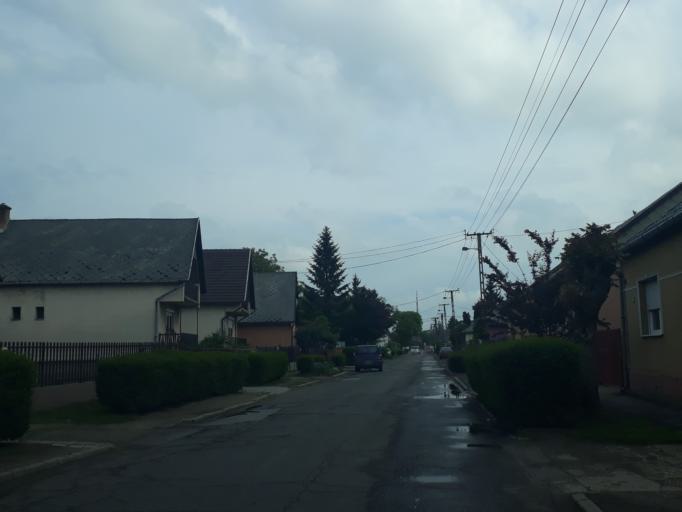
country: HU
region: Szabolcs-Szatmar-Bereg
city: Kisvarda
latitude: 48.2154
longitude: 22.0758
